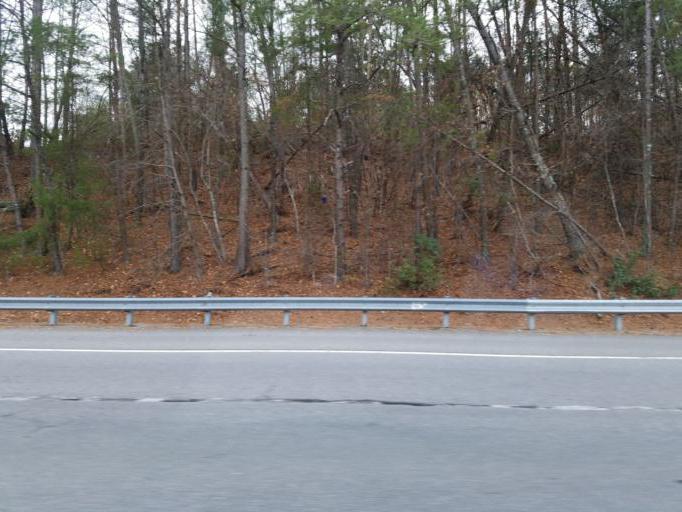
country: US
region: Georgia
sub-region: Cherokee County
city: Canton
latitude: 34.2199
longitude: -84.4921
